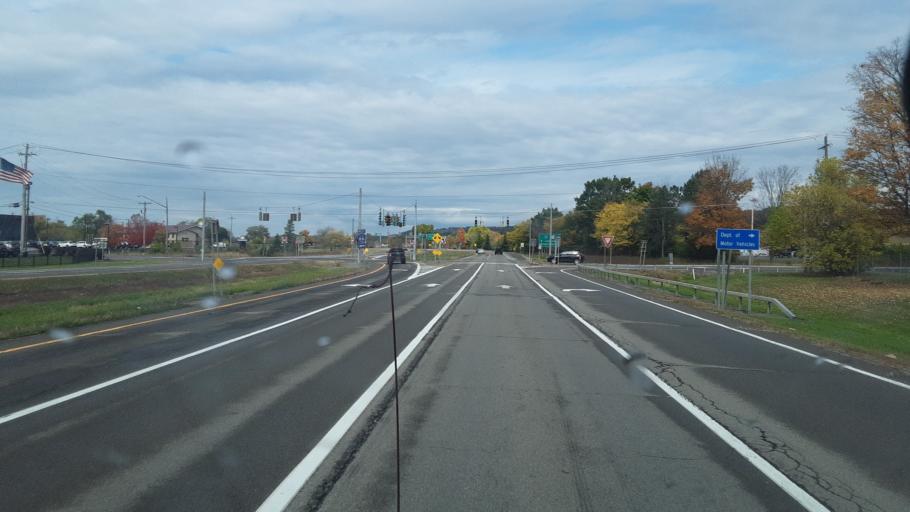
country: US
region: New York
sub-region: Steuben County
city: Hornell
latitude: 42.3651
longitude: -77.6736
